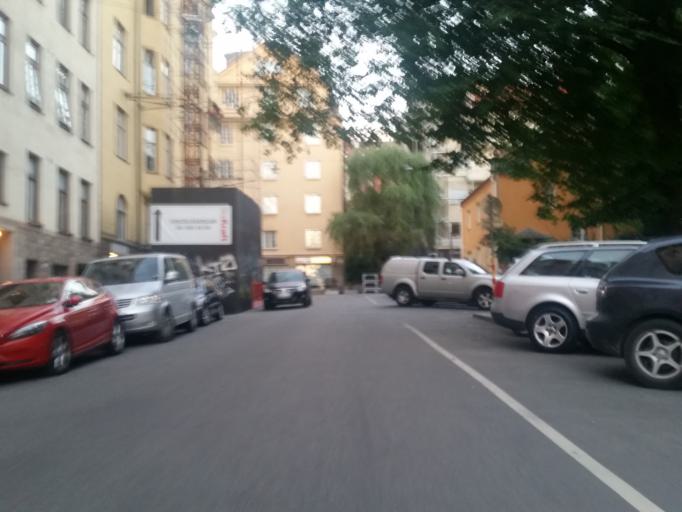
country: SE
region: Stockholm
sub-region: Stockholms Kommun
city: Stockholm
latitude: 59.3163
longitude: 18.0646
